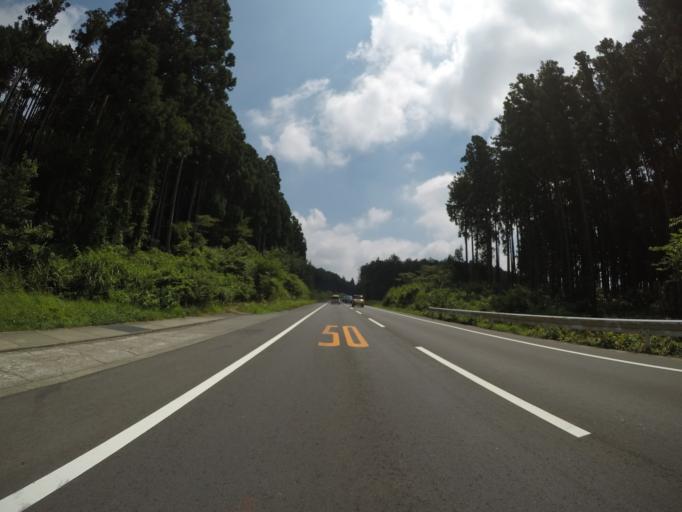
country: JP
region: Shizuoka
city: Fujinomiya
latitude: 35.2560
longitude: 138.6795
